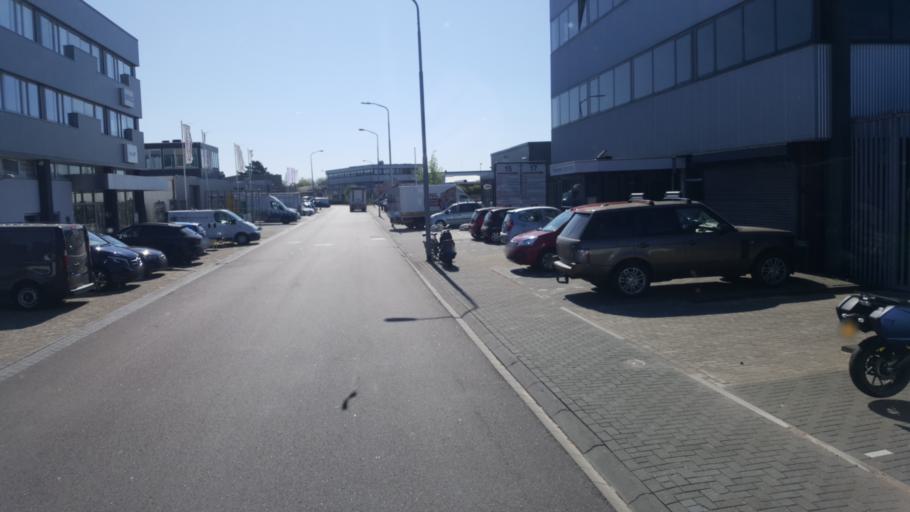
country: NL
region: North Holland
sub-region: Gemeente Haarlemmermeer
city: Hoofddorp
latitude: 52.3845
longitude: 4.7341
